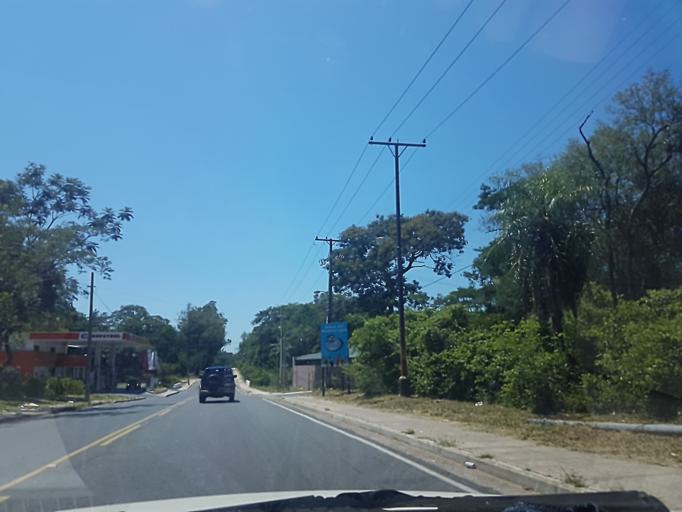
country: PY
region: Cordillera
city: San Bernardino
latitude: -25.2914
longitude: -57.3097
